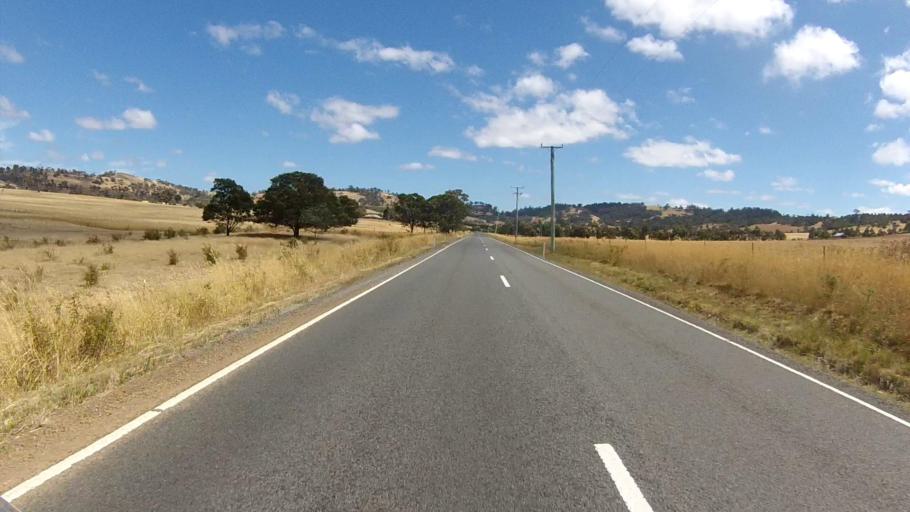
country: AU
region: Tasmania
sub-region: Sorell
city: Sorell
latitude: -42.7555
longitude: 147.5070
